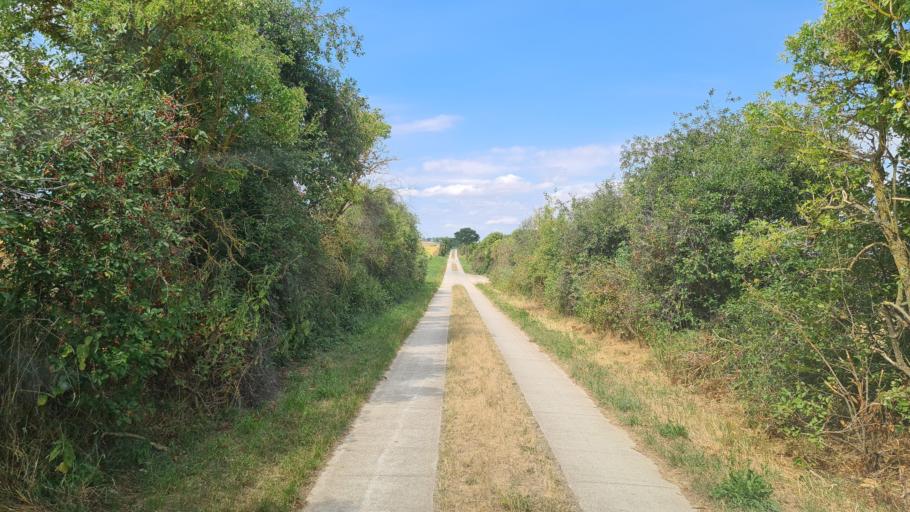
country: DE
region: Brandenburg
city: Juterbog
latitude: 51.9460
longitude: 13.1073
